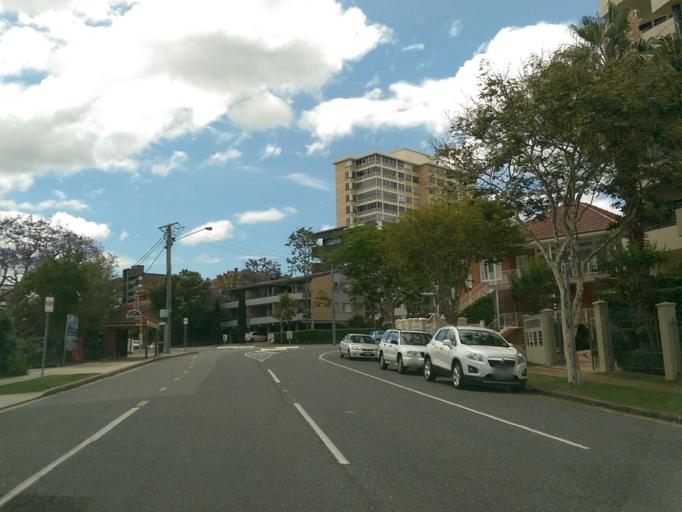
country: AU
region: Queensland
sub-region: Brisbane
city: Brisbane
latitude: -27.4668
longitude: 153.0411
